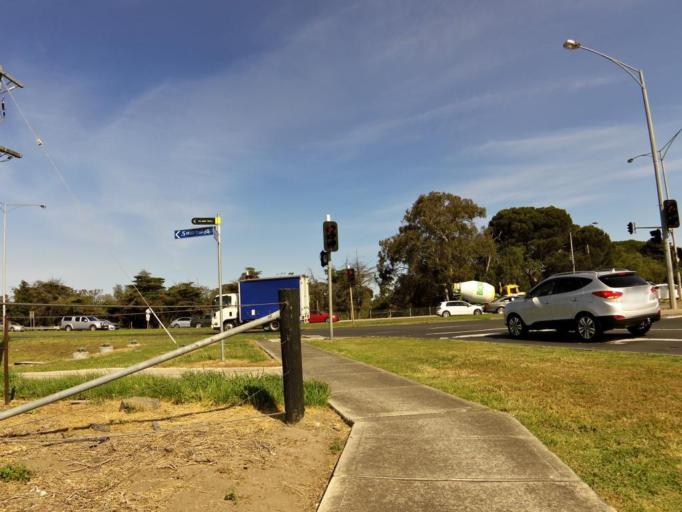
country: AU
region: Victoria
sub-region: Brimbank
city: Deer Park
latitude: -37.7703
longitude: 144.7903
